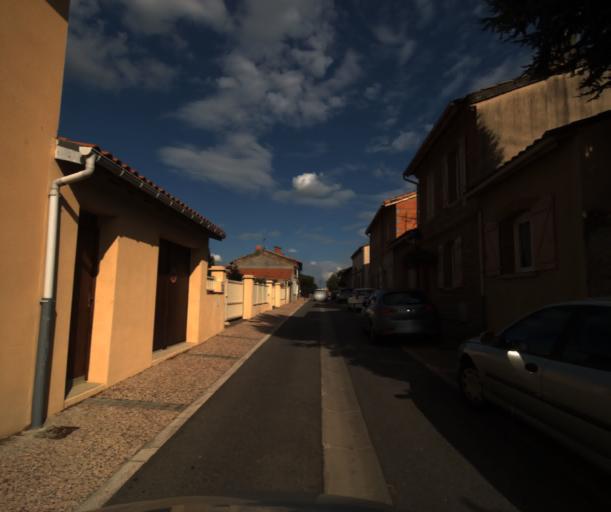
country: FR
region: Midi-Pyrenees
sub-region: Departement de la Haute-Garonne
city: Saubens
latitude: 43.4808
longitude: 1.3486
